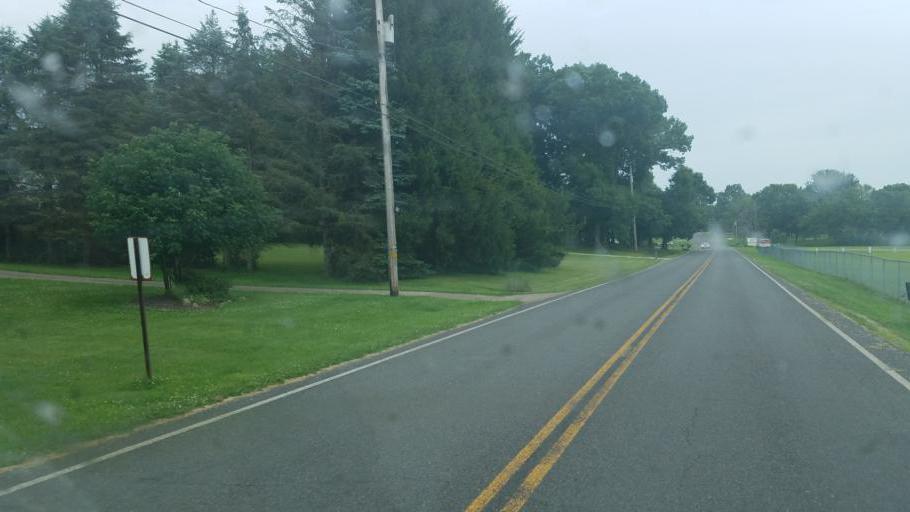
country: US
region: Ohio
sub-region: Summit County
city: Clinton
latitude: 40.9125
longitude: -81.6236
